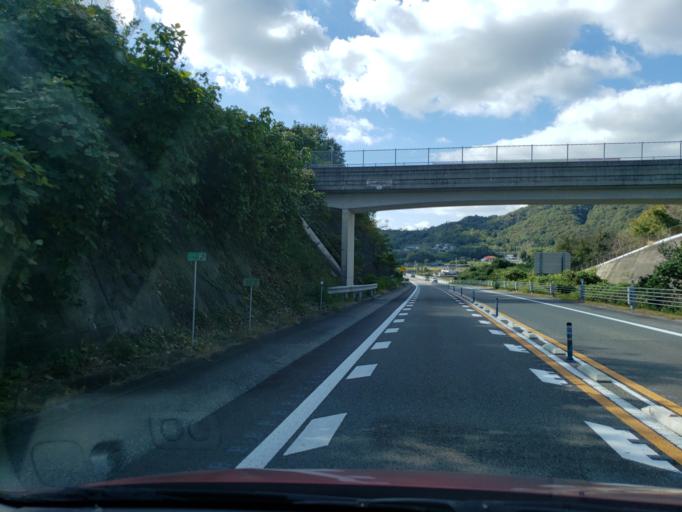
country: JP
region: Tokushima
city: Ishii
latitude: 34.1366
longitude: 134.3983
